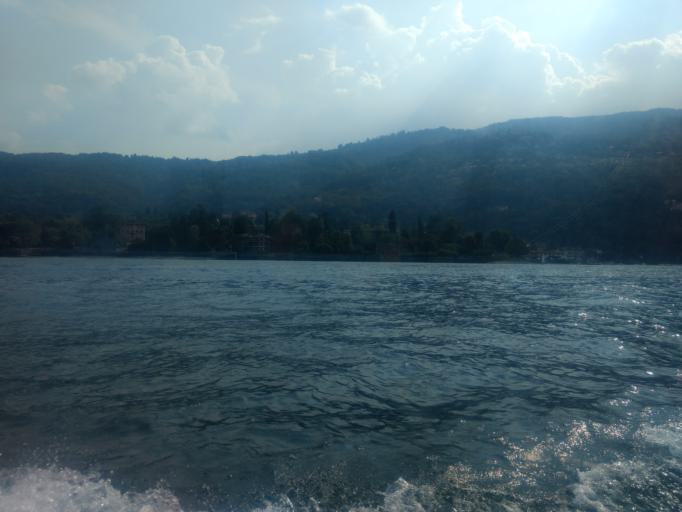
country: IT
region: Piedmont
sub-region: Provincia Verbano-Cusio-Ossola
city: Stresa
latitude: 45.8927
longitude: 8.5297
